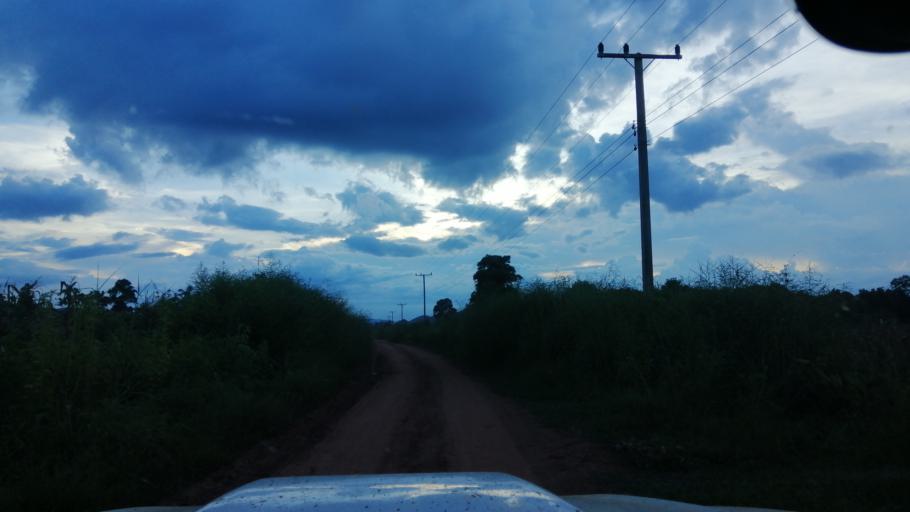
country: TH
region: Uttaradit
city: Ban Khok
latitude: 17.8785
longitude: 101.0594
